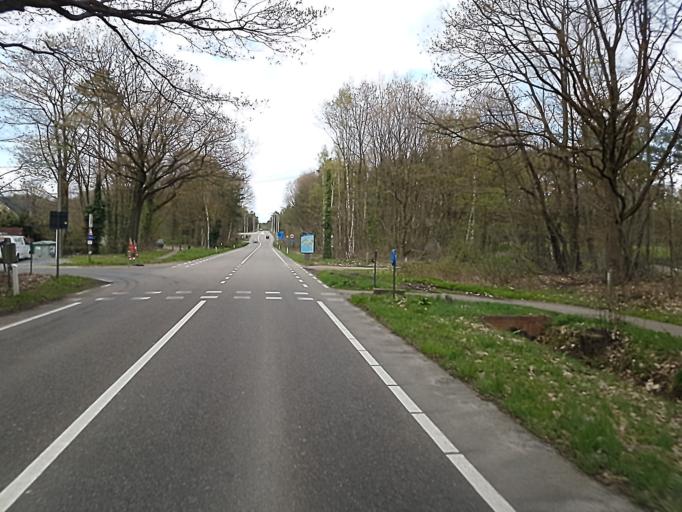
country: BE
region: Flanders
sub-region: Provincie Limburg
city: Zutendaal
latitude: 50.9714
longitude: 5.5523
